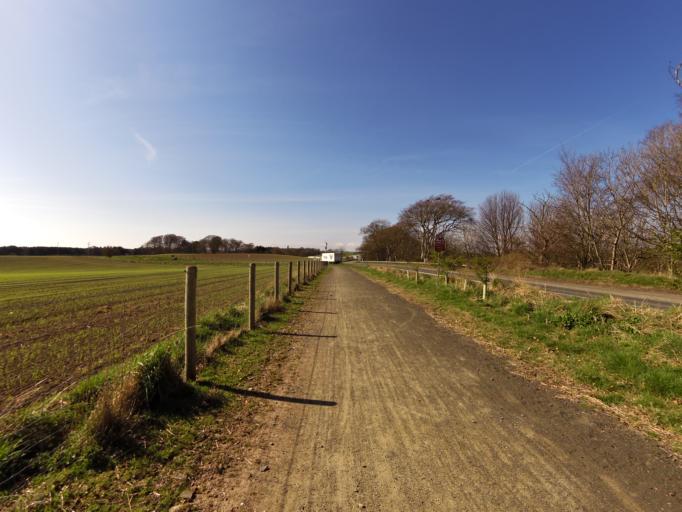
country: GB
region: Scotland
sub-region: Angus
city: Montrose
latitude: 56.7478
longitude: -2.4531
